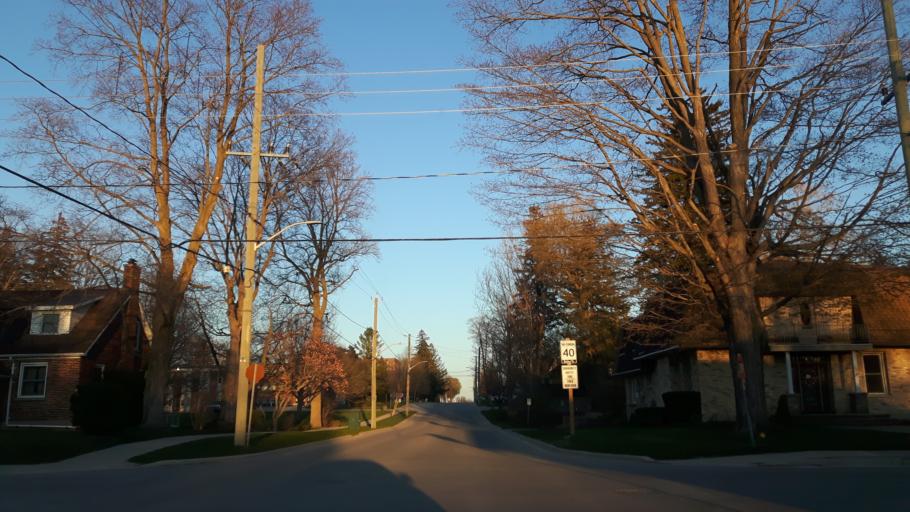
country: CA
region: Ontario
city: Bluewater
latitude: 43.6176
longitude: -81.5360
